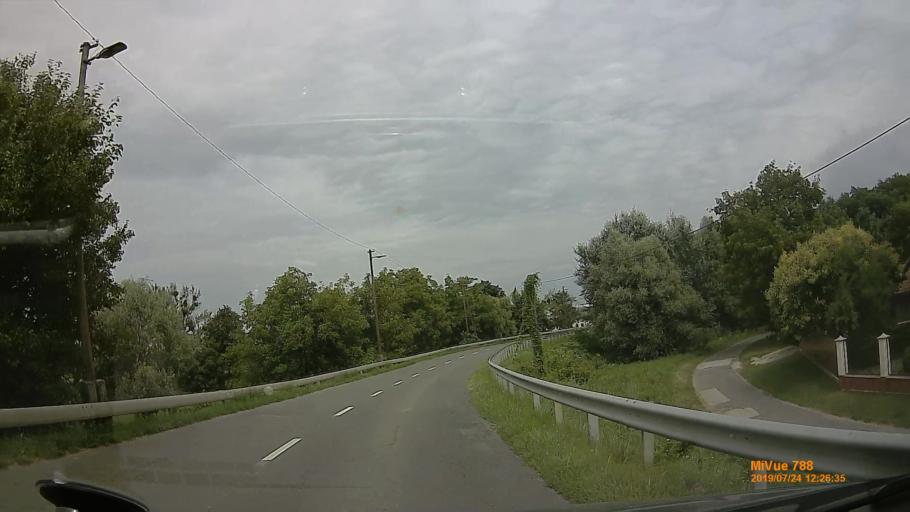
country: HU
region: Szabolcs-Szatmar-Bereg
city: Vasarosnameny
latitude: 48.1302
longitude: 22.3418
